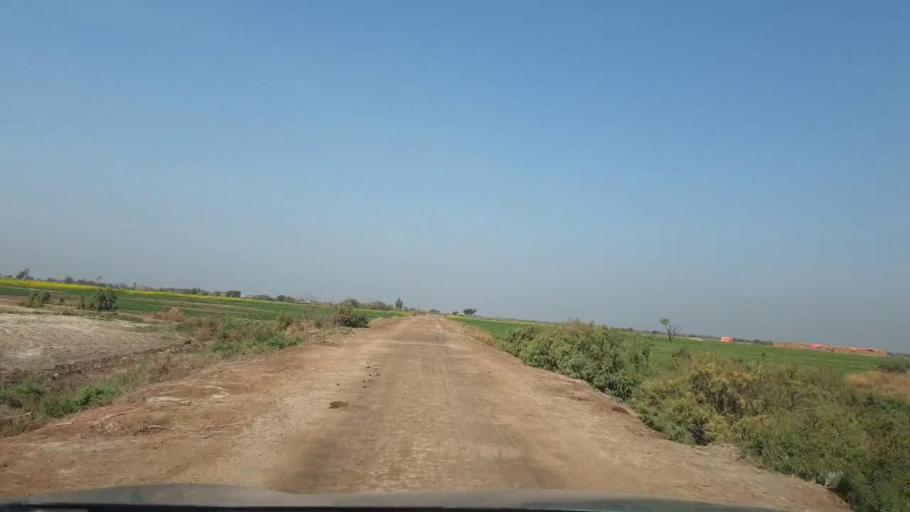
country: PK
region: Sindh
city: Berani
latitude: 25.7061
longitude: 68.8648
